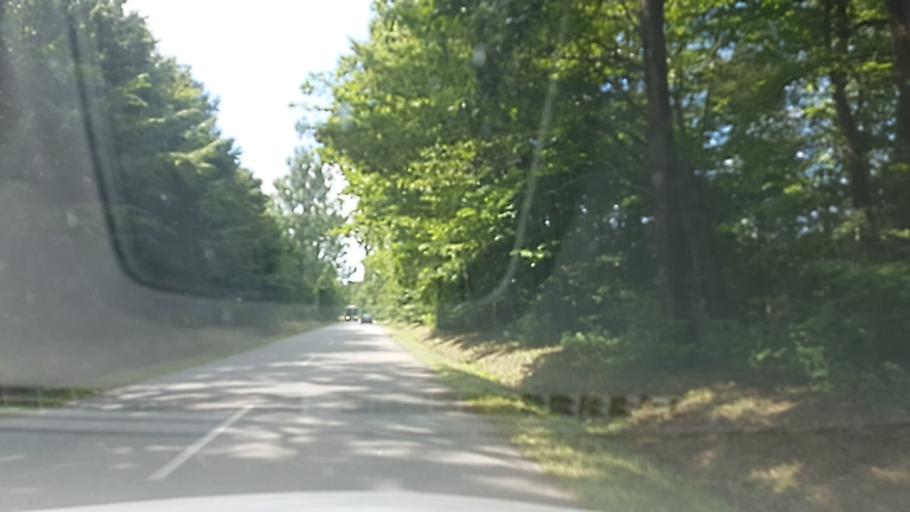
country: HU
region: Somogy
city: Barcs
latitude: 45.9454
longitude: 17.6317
